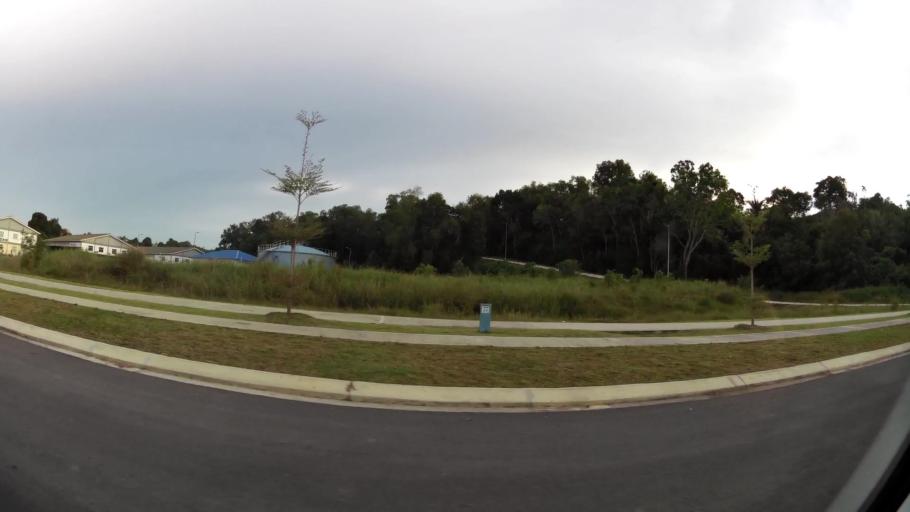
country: BN
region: Brunei and Muara
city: Bandar Seri Begawan
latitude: 4.9865
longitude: 114.9843
